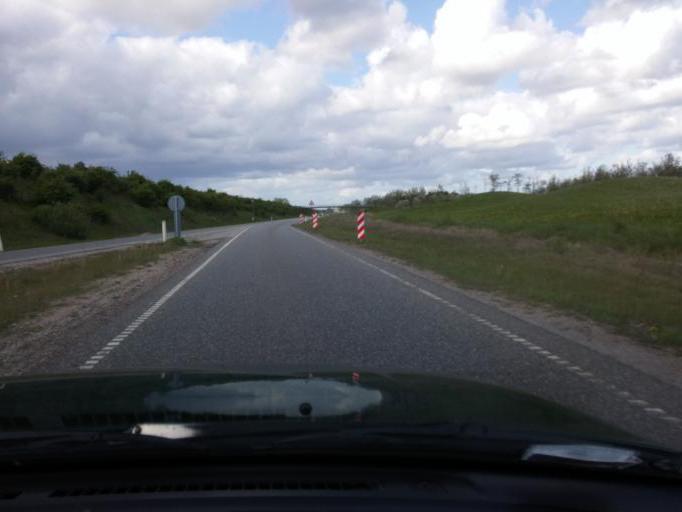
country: DK
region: South Denmark
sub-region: Odense Kommune
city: Neder Holluf
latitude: 55.3665
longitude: 10.4698
